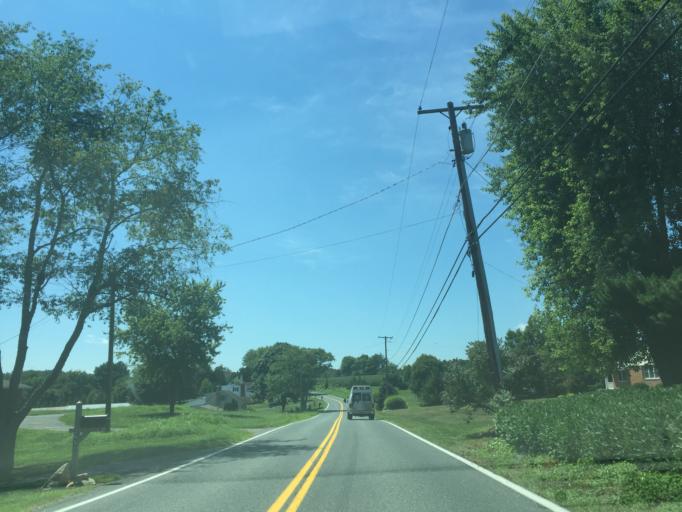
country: US
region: Maryland
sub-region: Harford County
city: Bel Air North
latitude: 39.6084
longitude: -76.3855
